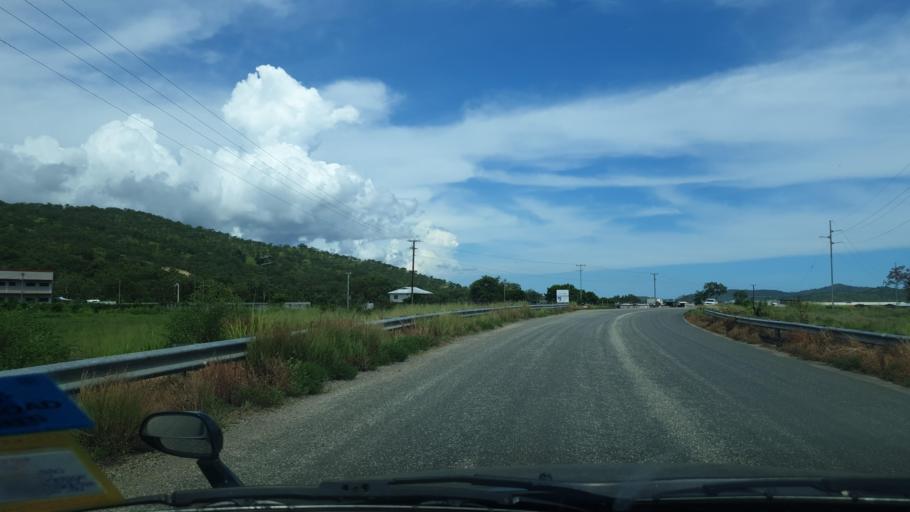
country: PG
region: National Capital
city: Port Moresby
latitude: -9.4091
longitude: 147.0711
